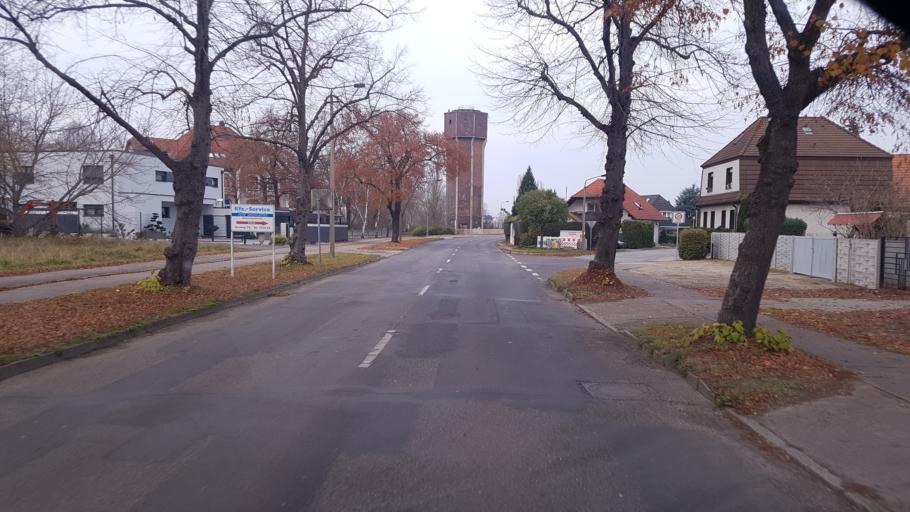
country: DE
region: Brandenburg
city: Eisenhuettenstadt
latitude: 52.1494
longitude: 14.6740
